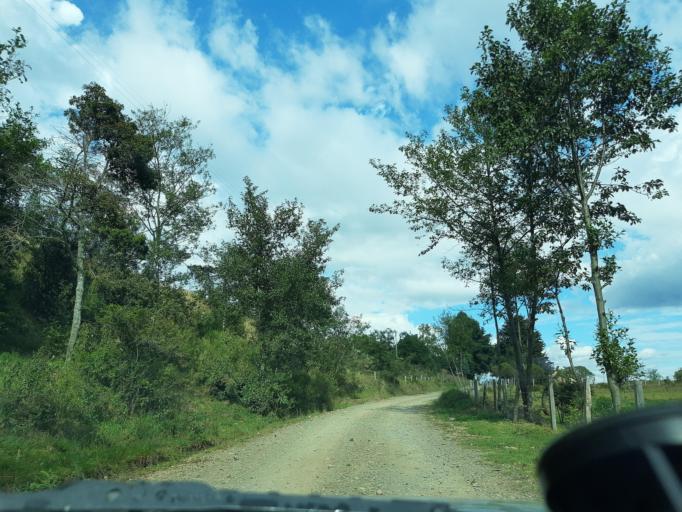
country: CO
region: Boyaca
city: Raquira
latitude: 5.5095
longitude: -73.6684
